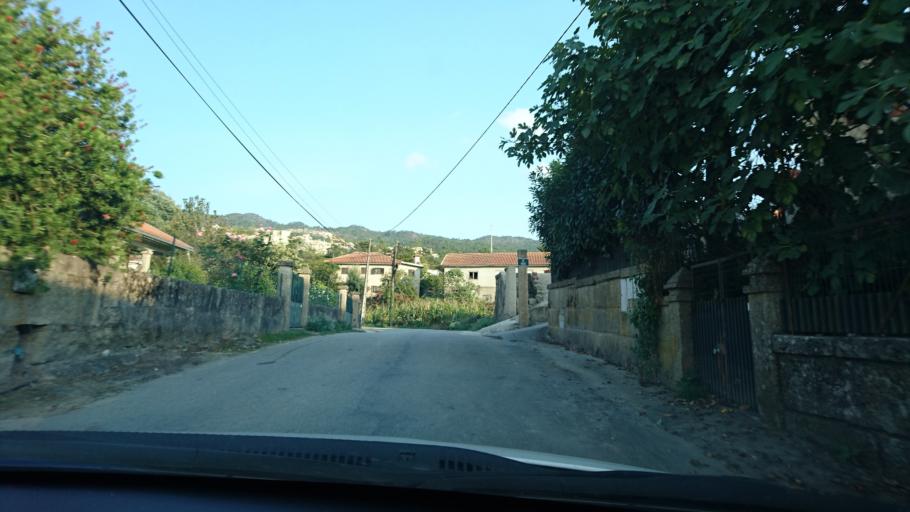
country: PT
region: Vila Real
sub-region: Mondim de Basto
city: Mondim de Basto
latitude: 41.4438
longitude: -7.9276
